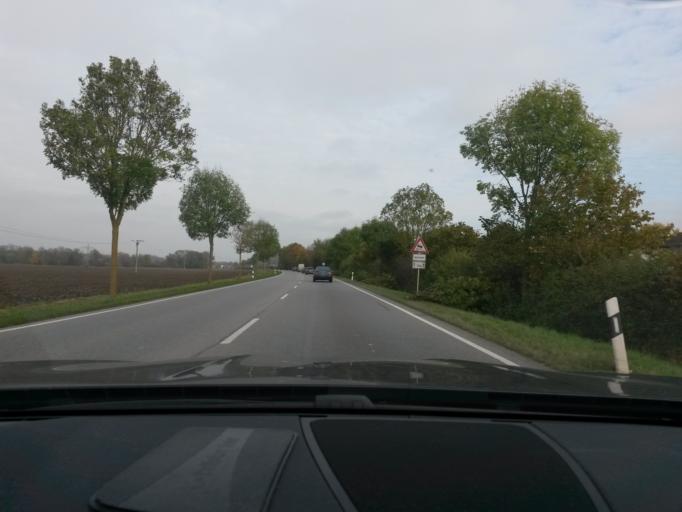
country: DE
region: Bavaria
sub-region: Lower Bavaria
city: Eching
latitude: 48.5003
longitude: 12.0627
